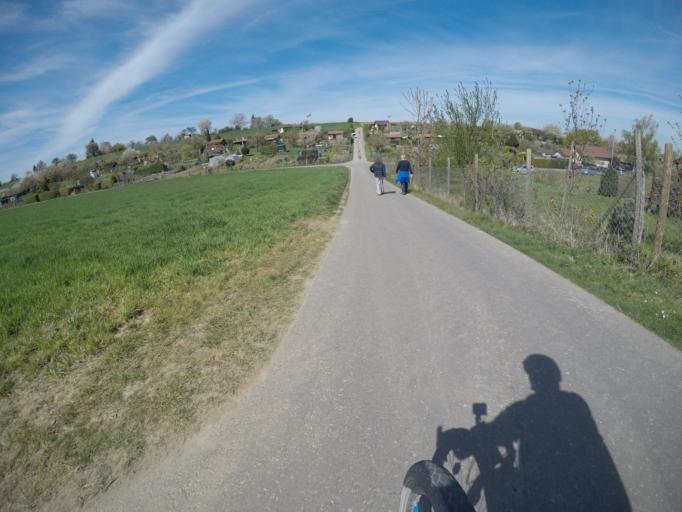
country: DE
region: Baden-Wuerttemberg
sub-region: Regierungsbezirk Stuttgart
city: Leonberg
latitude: 48.8228
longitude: 9.0232
